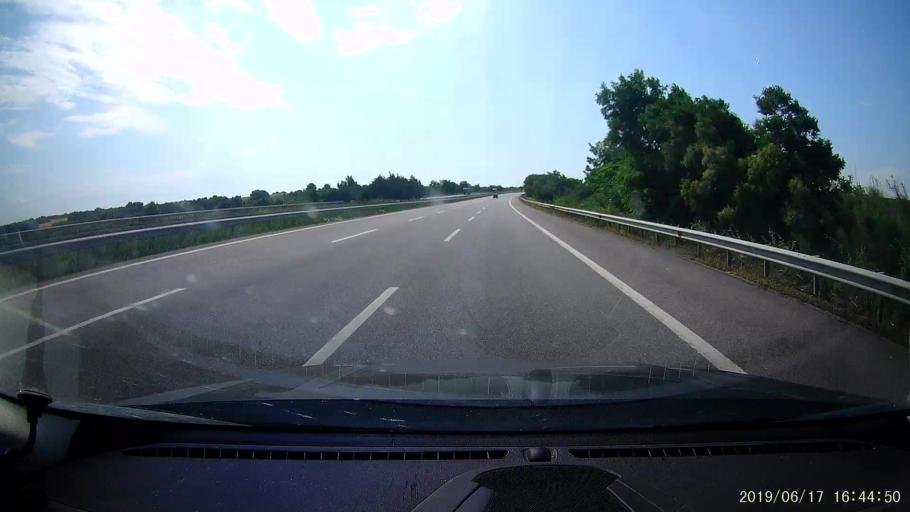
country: TR
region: Kirklareli
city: Luleburgaz
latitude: 41.4826
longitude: 27.2492
